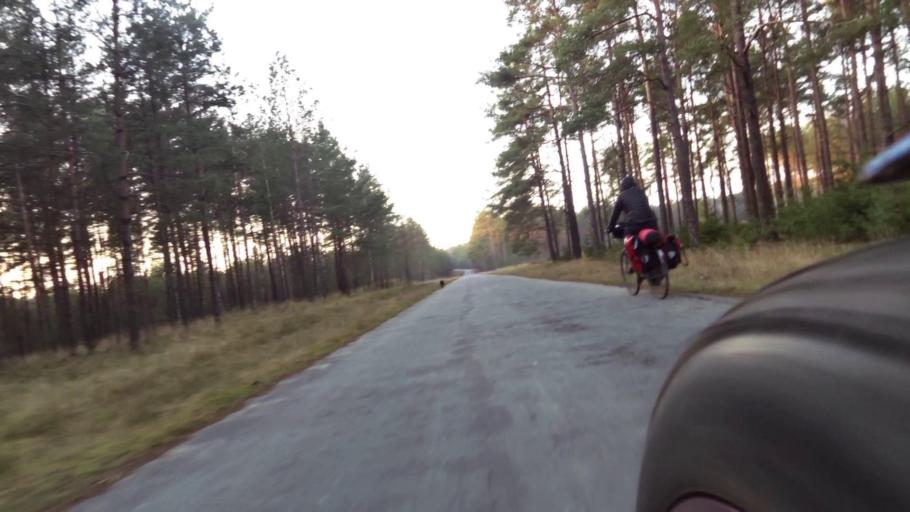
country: PL
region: West Pomeranian Voivodeship
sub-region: Powiat szczecinecki
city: Borne Sulinowo
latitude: 53.5669
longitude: 16.5928
